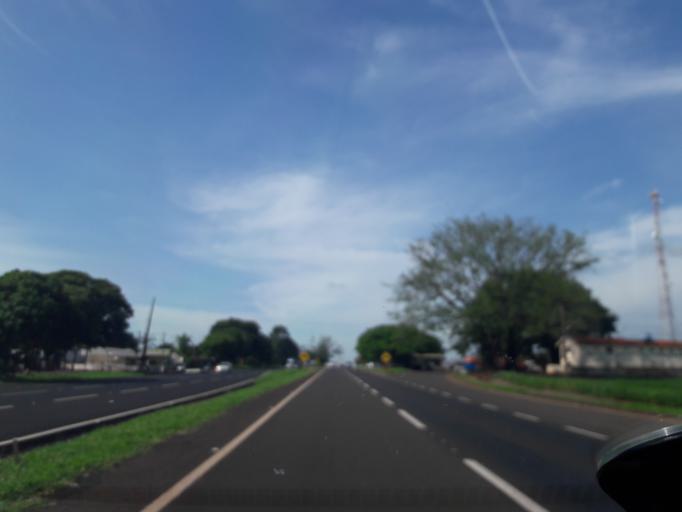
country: BR
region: Parana
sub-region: Paicandu
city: Paicandu
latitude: -23.6086
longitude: -52.0861
